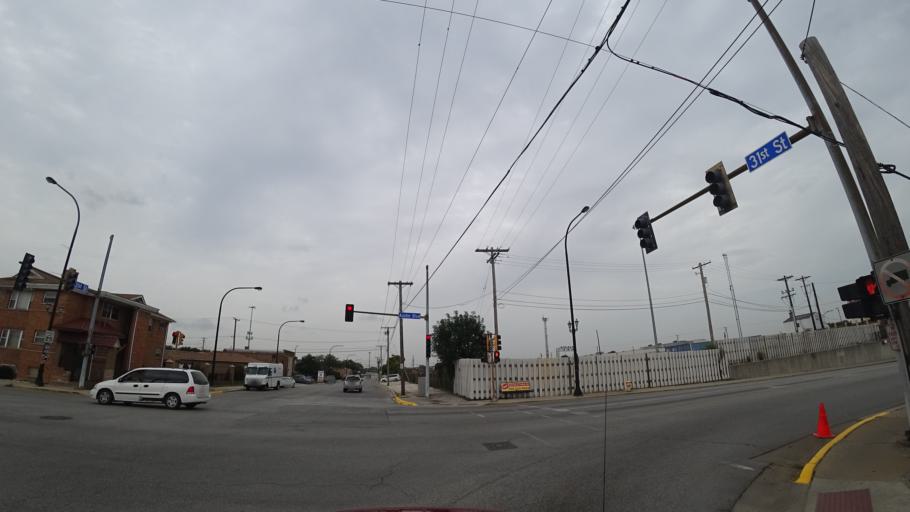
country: US
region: Illinois
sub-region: Cook County
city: Stickney
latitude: 41.8363
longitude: -87.7731
